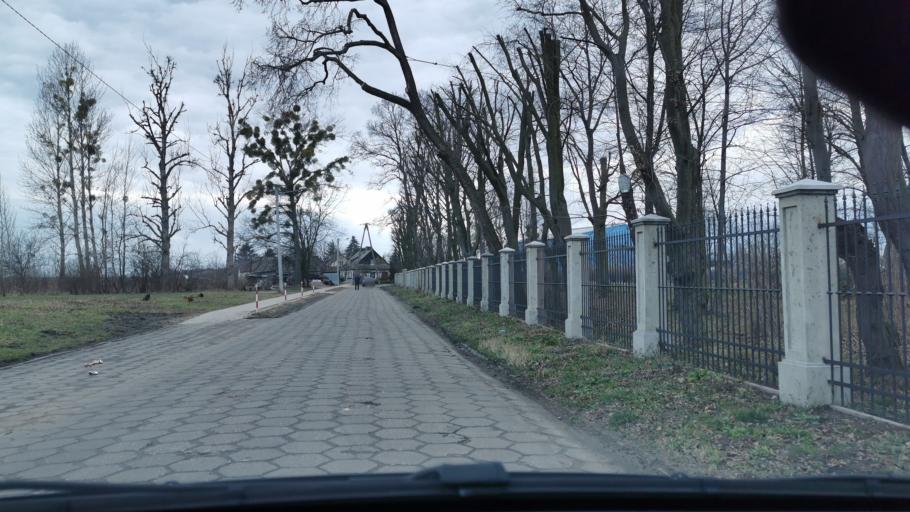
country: PL
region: Masovian Voivodeship
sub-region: Powiat zyrardowski
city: Guzow
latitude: 52.1124
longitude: 20.3353
